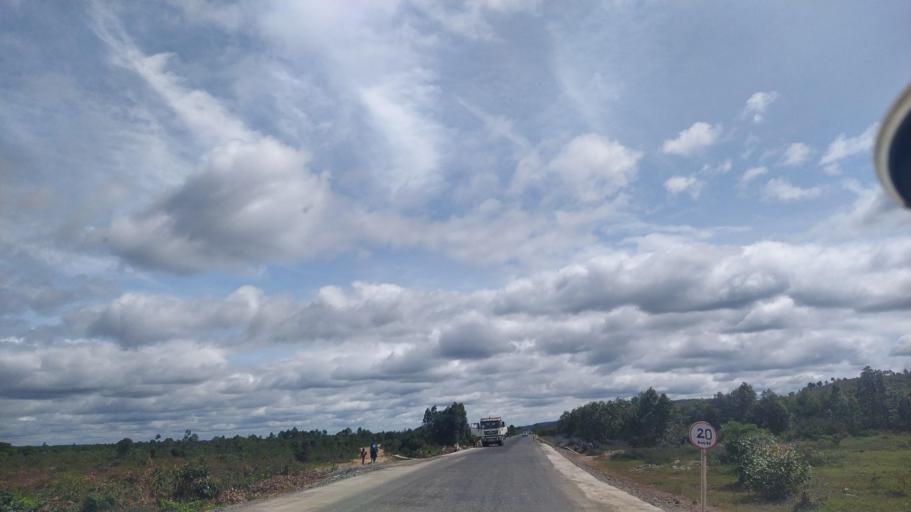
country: MG
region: Alaotra Mangoro
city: Moramanga
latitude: -18.6879
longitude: 48.2720
